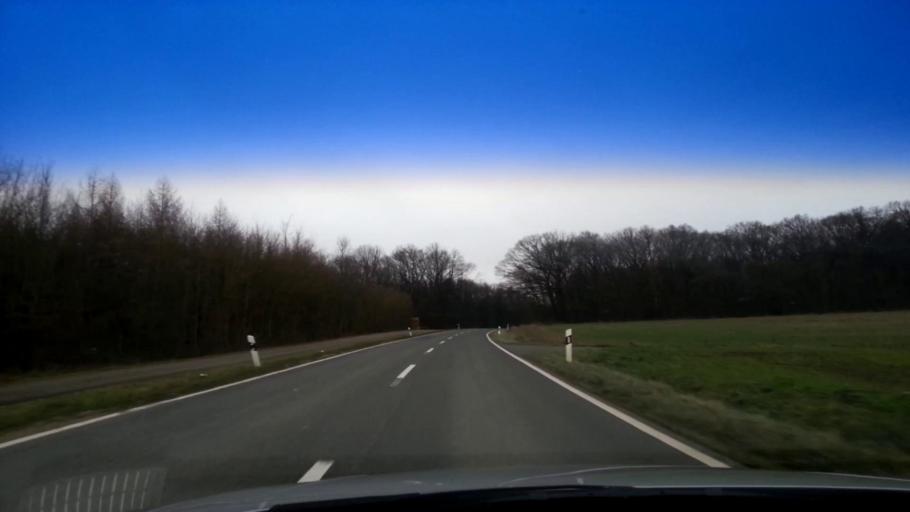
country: DE
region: Bavaria
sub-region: Upper Franconia
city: Litzendorf
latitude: 49.8899
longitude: 11.0098
